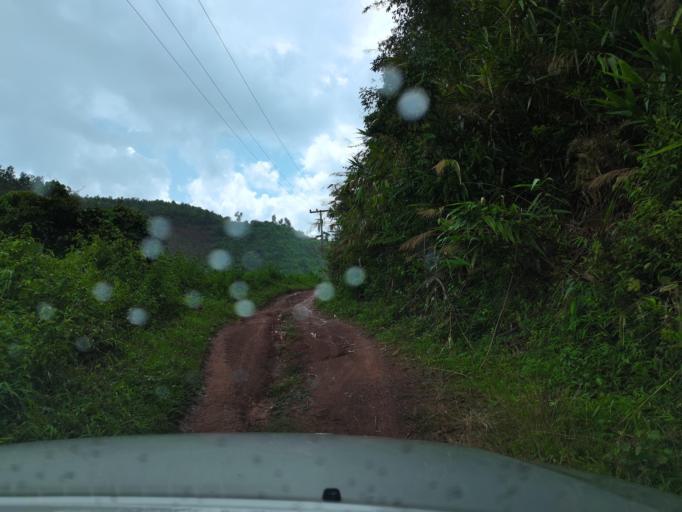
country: LA
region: Loungnamtha
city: Muang Nale
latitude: 20.5214
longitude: 101.0708
